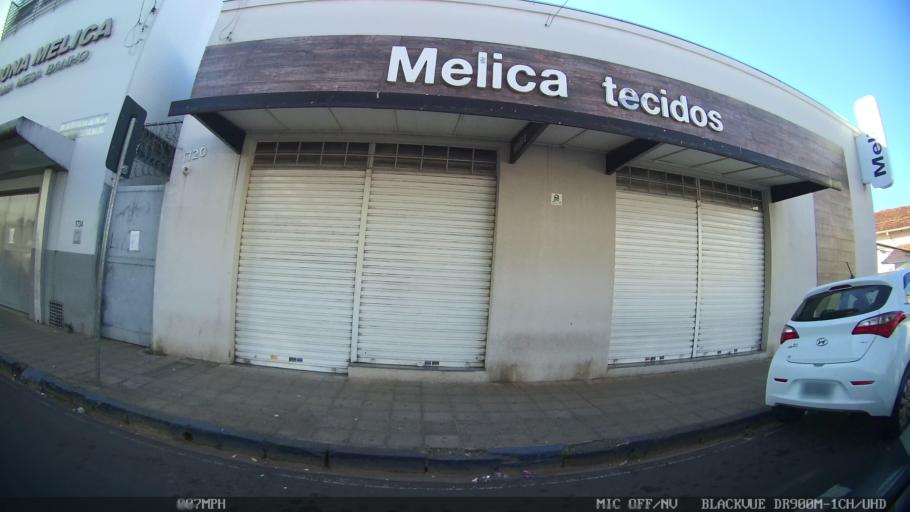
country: BR
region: Sao Paulo
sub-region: Franca
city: Franca
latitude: -20.5385
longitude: -47.4033
